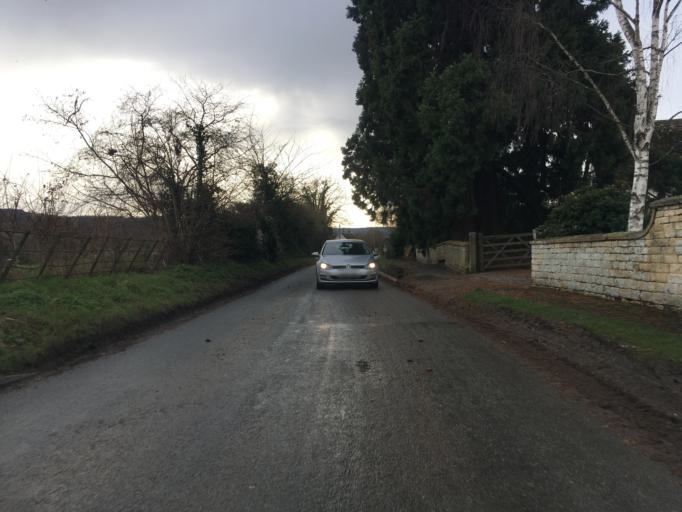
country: GB
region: England
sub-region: Worcestershire
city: Evesham
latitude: 52.0362
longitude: -2.0063
